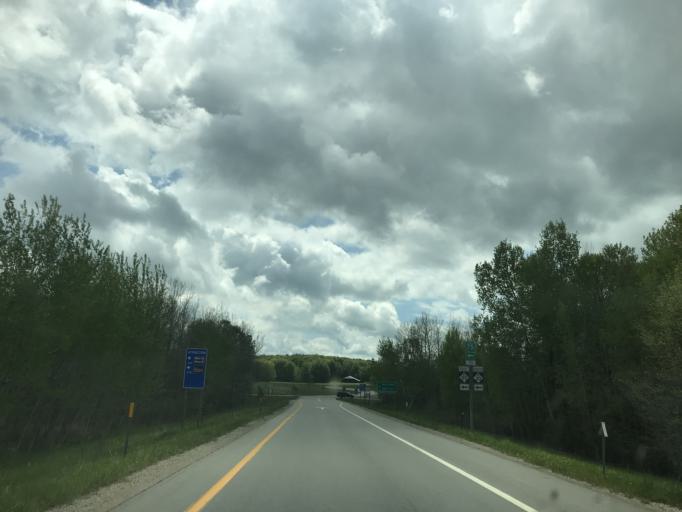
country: US
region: Michigan
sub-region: Ogemaw County
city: West Branch
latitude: 44.2780
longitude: -84.2857
